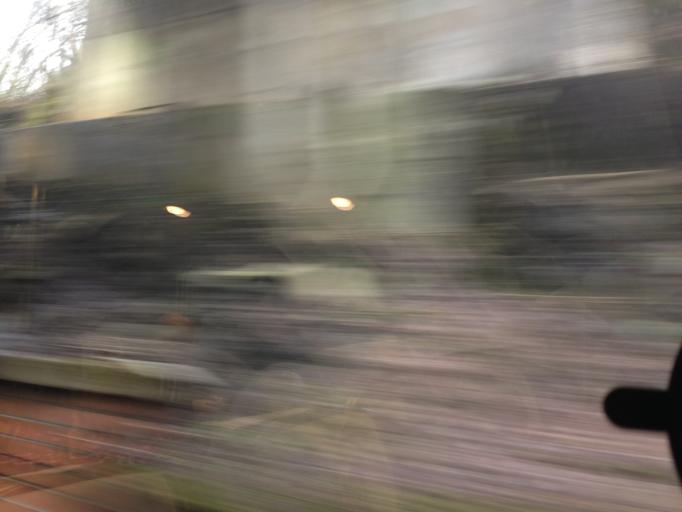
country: GB
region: Scotland
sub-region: Argyll and Bute
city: Garelochhead
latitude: 56.1625
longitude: -4.7807
